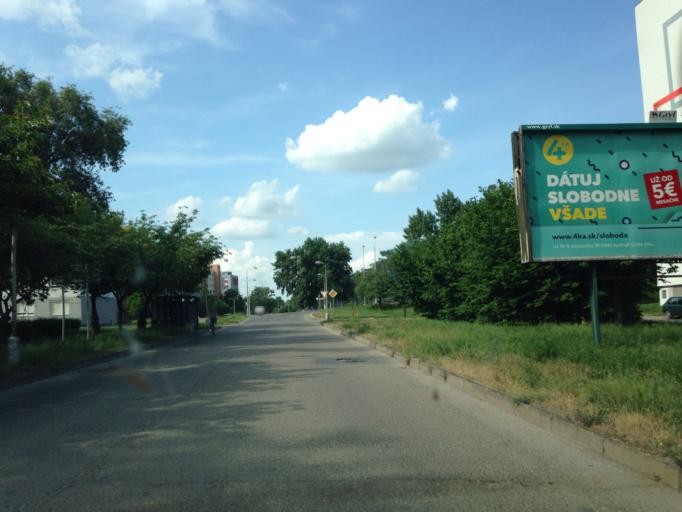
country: SK
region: Nitriansky
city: Komarno
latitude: 47.7617
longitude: 18.1394
